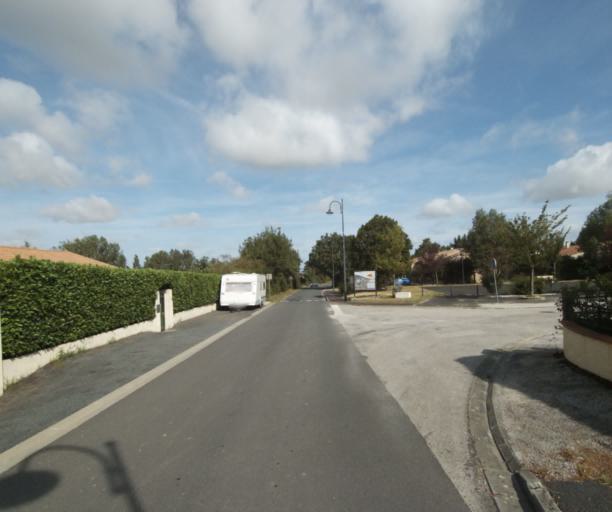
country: FR
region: Midi-Pyrenees
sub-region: Departement du Tarn
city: Soreze
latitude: 43.4687
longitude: 2.0794
